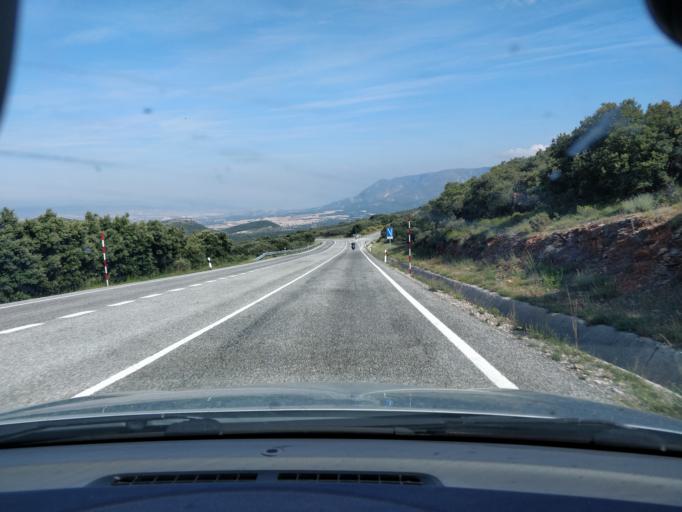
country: ES
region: Castille and Leon
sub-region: Provincia de Burgos
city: Medina de Pomar
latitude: 42.9215
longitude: -3.6243
